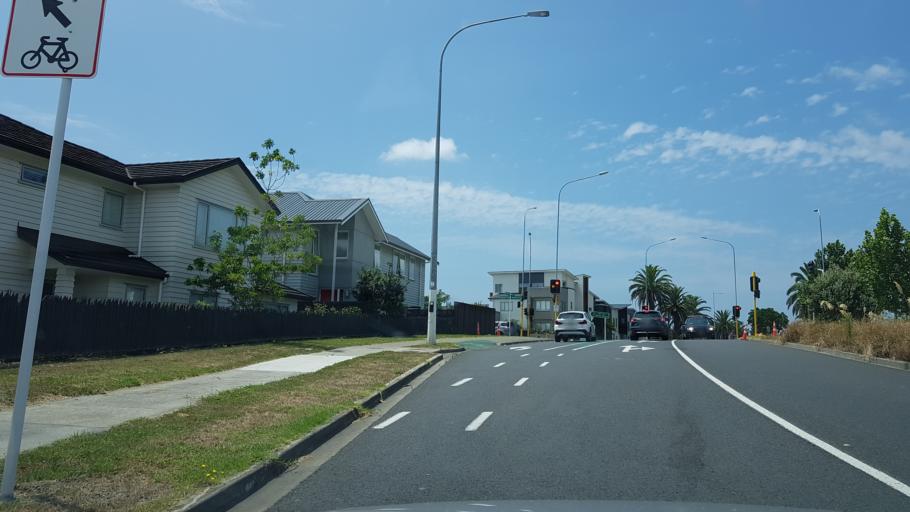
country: NZ
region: Auckland
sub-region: Auckland
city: Rosebank
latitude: -36.7929
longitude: 174.6550
